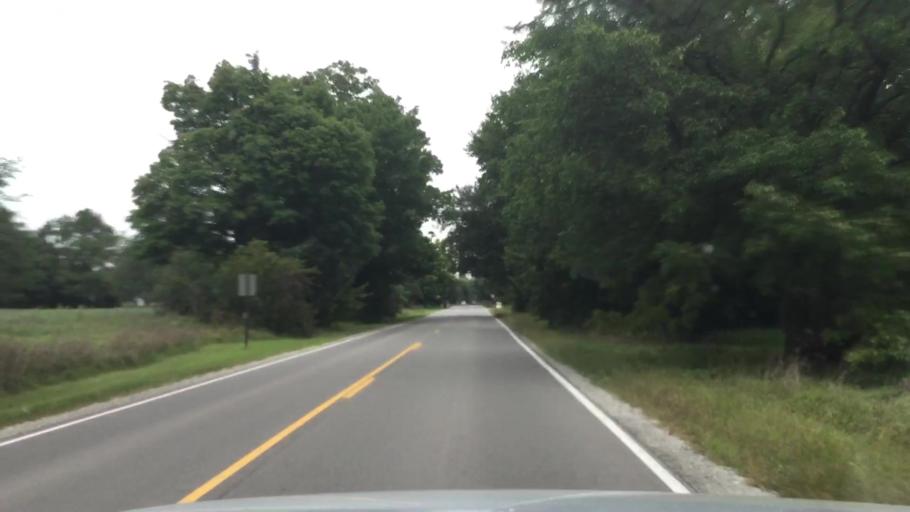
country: US
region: Michigan
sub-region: Washtenaw County
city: Ypsilanti
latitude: 42.1903
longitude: -83.6340
